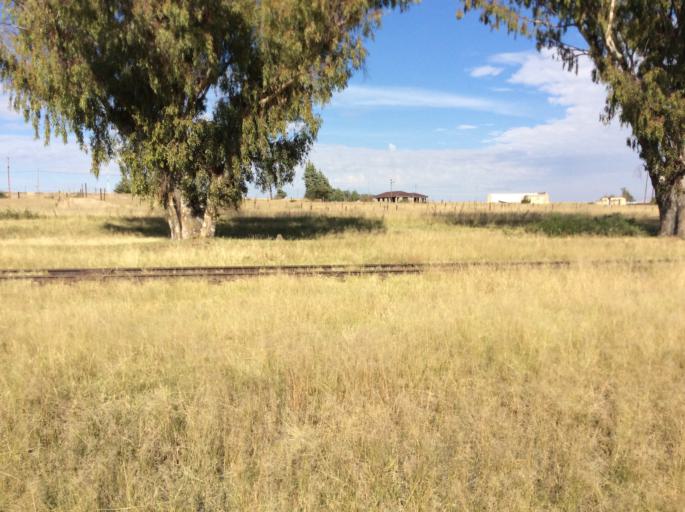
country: LS
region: Mafeteng
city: Mafeteng
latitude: -29.7330
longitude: 27.0295
